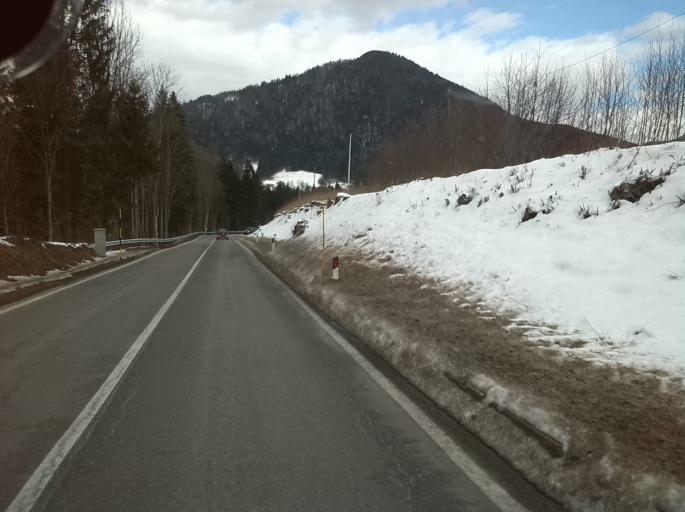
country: IT
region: Friuli Venezia Giulia
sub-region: Provincia di Udine
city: Tarvisio
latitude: 46.5050
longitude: 13.6166
